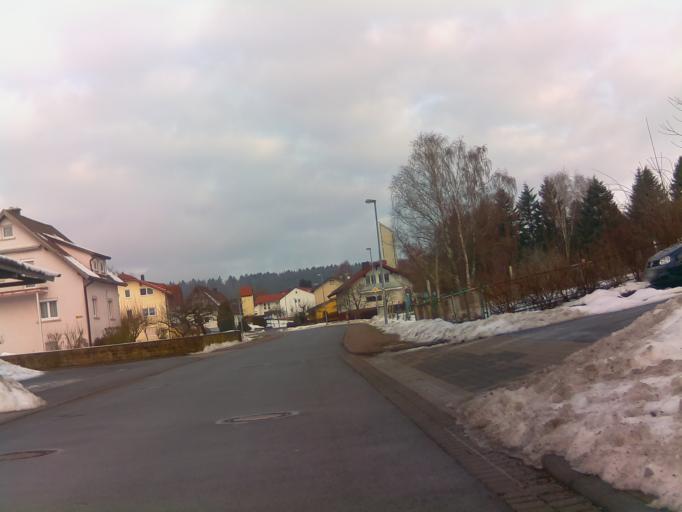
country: DE
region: Baden-Wuerttemberg
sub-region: Karlsruhe Region
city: Limbach
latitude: 49.4783
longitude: 9.1742
